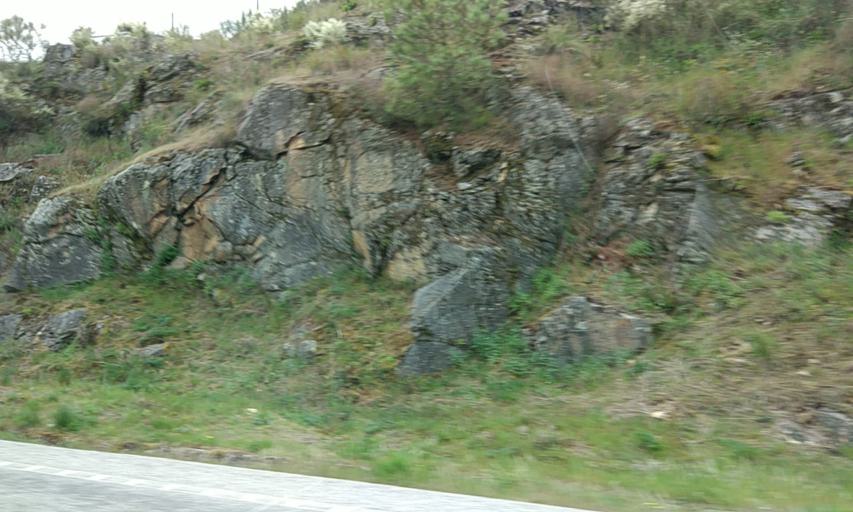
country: PT
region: Guarda
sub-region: Guarda
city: Guarda
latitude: 40.5878
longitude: -7.2748
